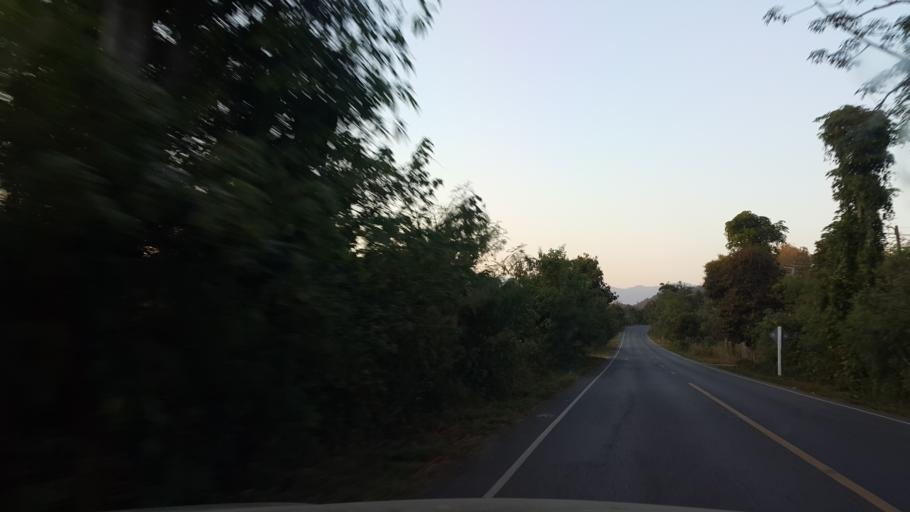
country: TH
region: Phrae
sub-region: Amphoe Wang Chin
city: Wang Chin
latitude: 17.8354
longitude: 99.6420
